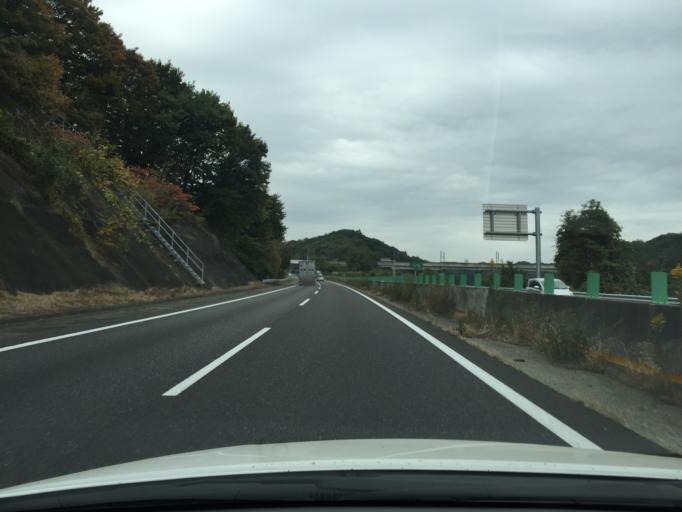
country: JP
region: Fukushima
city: Sukagawa
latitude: 37.1478
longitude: 140.2180
